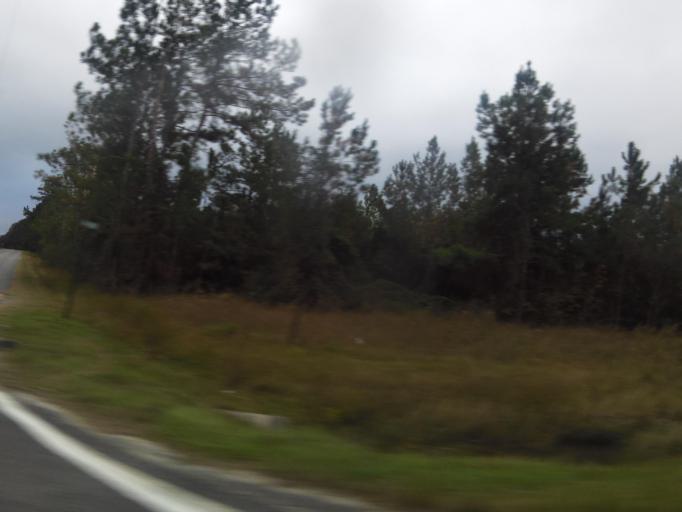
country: US
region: Georgia
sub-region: Charlton County
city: Folkston
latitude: 30.7809
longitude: -82.0507
